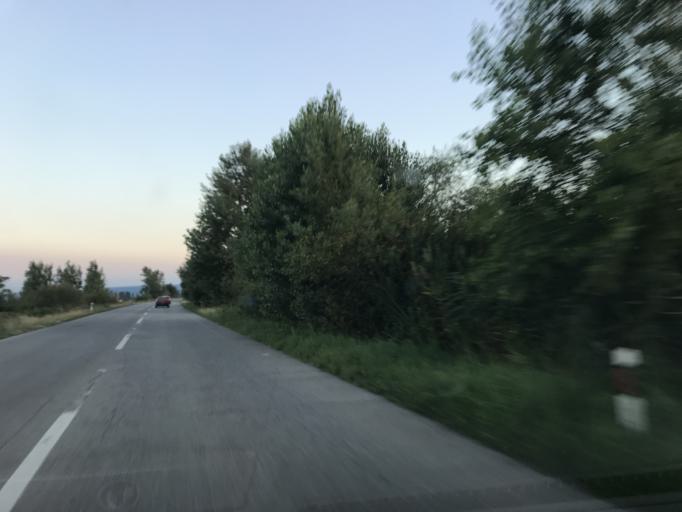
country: RS
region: Central Serbia
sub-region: Borski Okrug
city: Negotin
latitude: 44.2574
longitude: 22.5193
